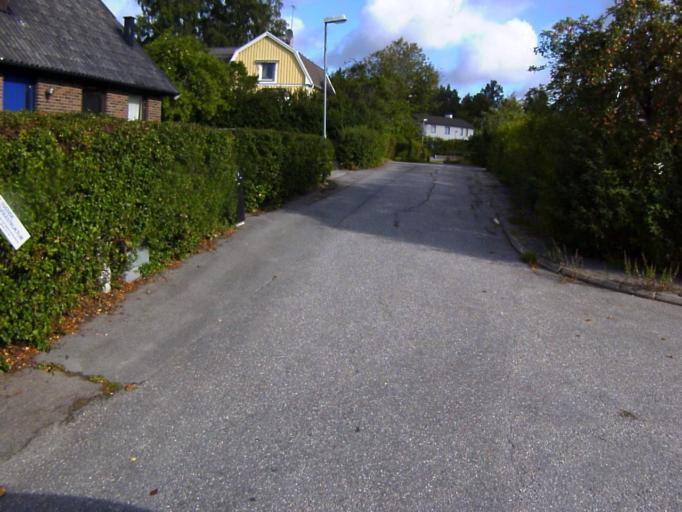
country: SE
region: Soedermanland
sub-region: Eskilstuna Kommun
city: Eskilstuna
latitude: 59.3774
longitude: 16.5531
